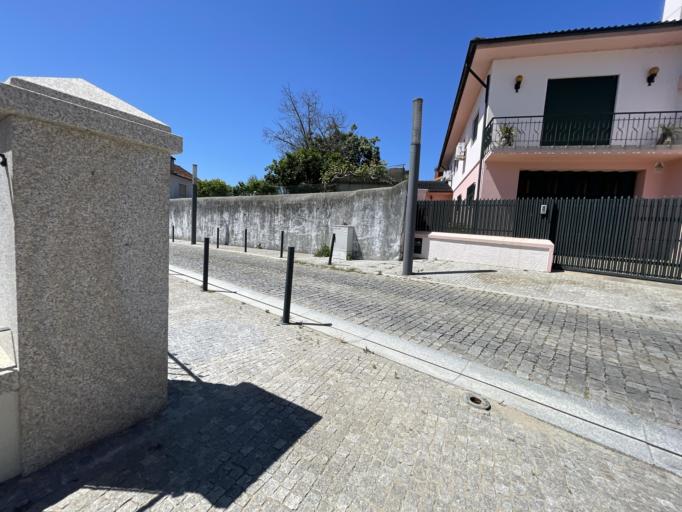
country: PT
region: Aveiro
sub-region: Ovar
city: Cortegaca
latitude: 40.9433
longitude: -8.6253
